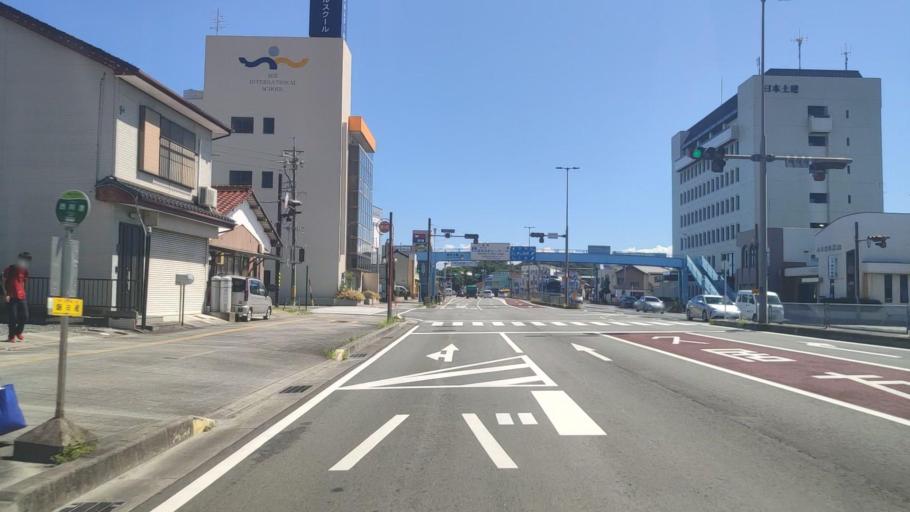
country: JP
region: Mie
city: Tsu-shi
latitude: 34.7053
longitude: 136.5071
